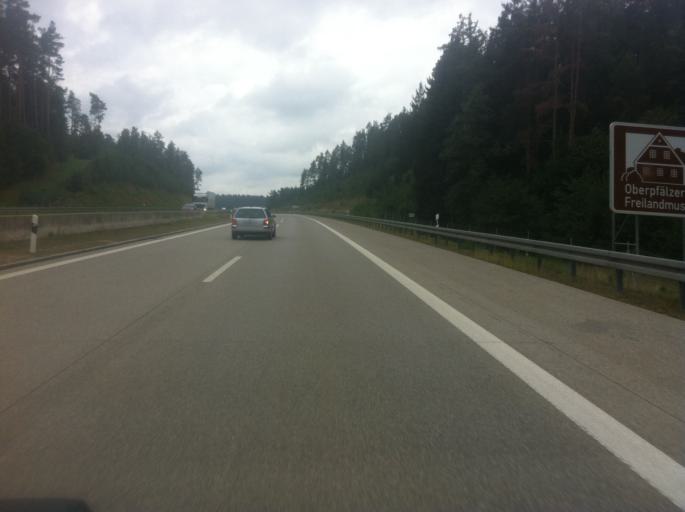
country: DE
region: Bavaria
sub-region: Upper Palatinate
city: Pfreimd
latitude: 49.4905
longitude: 12.1417
